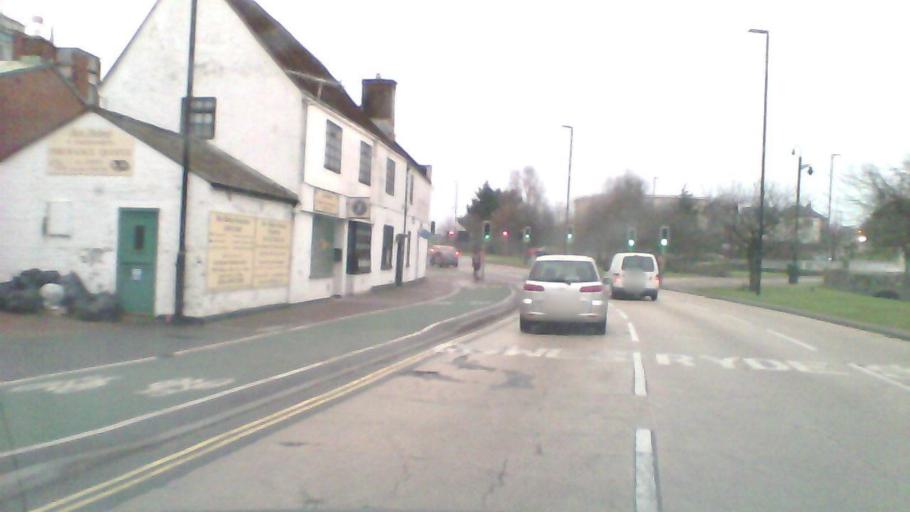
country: GB
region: England
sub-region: Isle of Wight
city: Newport
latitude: 50.7001
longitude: -1.2897
